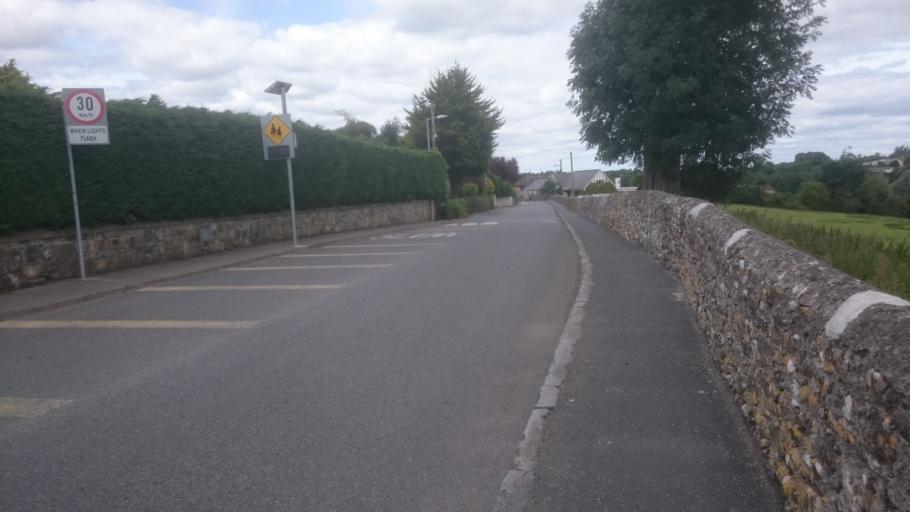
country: IE
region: Leinster
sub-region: Kilkenny
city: Kilkenny
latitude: 52.5382
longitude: -7.2704
